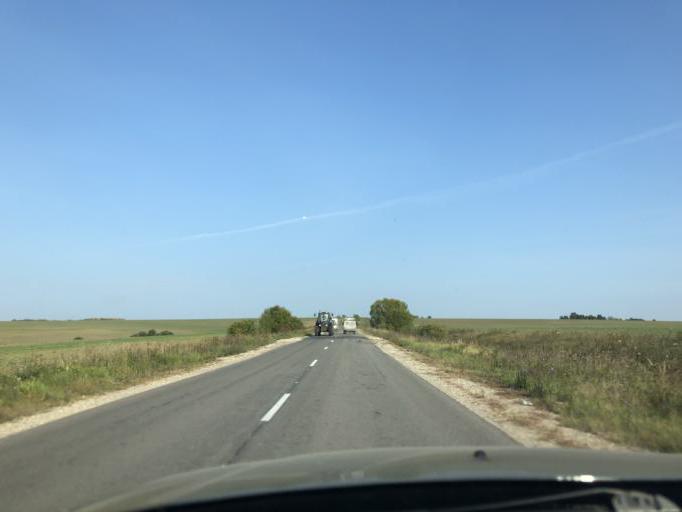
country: RU
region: Tula
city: Novogurovskiy
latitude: 54.3966
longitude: 37.3168
